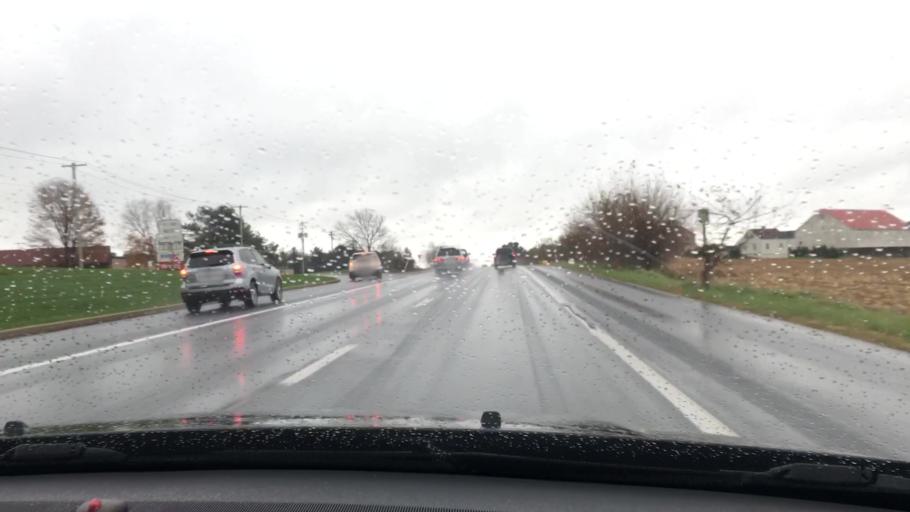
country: US
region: Pennsylvania
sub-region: Lancaster County
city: Willow Street
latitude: 39.9846
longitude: -76.2831
